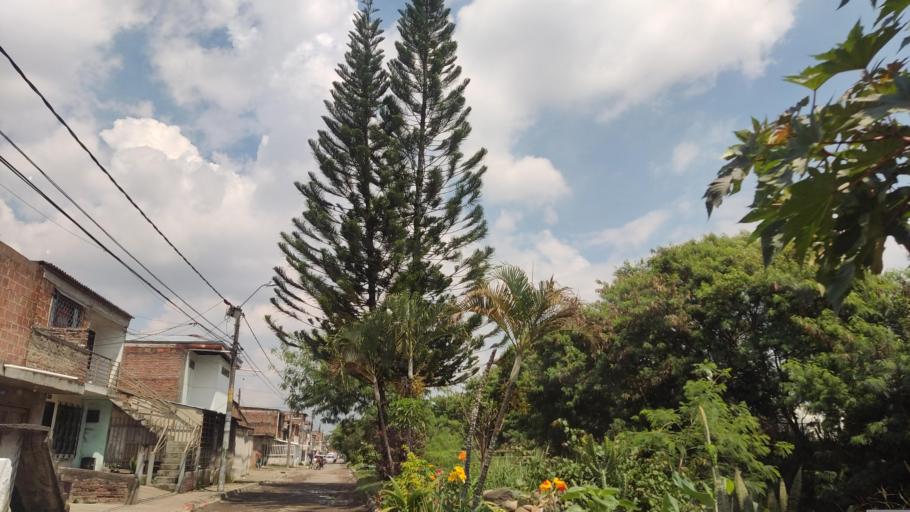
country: CO
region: Valle del Cauca
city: Cali
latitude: 3.4138
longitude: -76.5220
